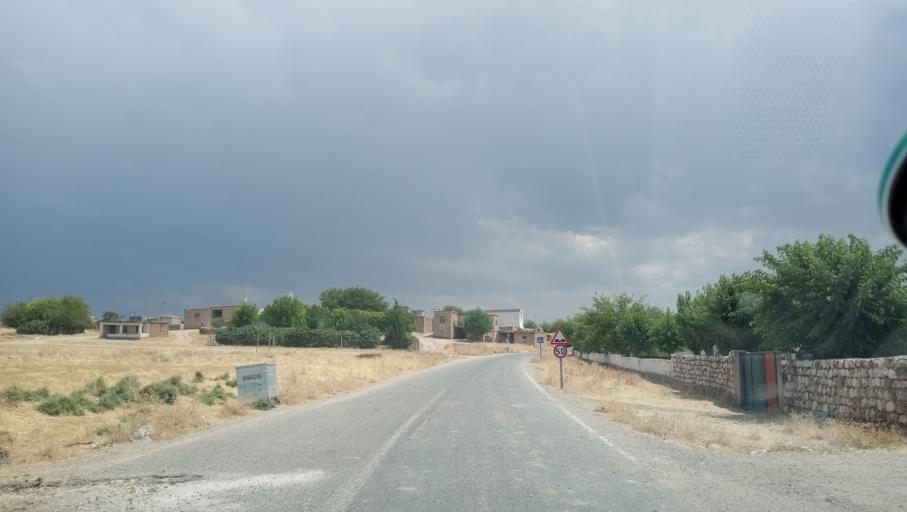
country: TR
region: Mardin
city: Baskavak
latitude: 37.6820
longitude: 40.8472
